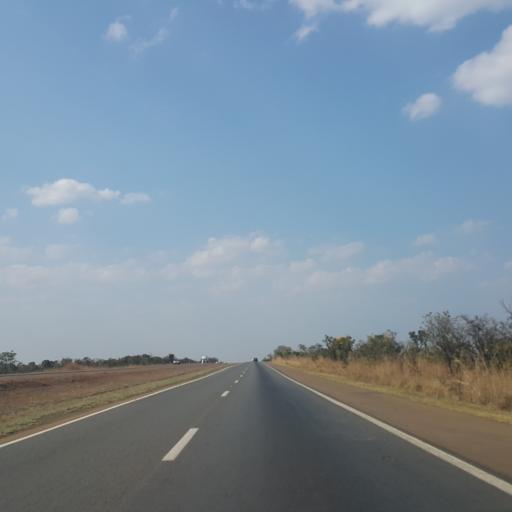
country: BR
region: Goias
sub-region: Abadiania
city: Abadiania
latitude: -16.2013
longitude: -48.7372
